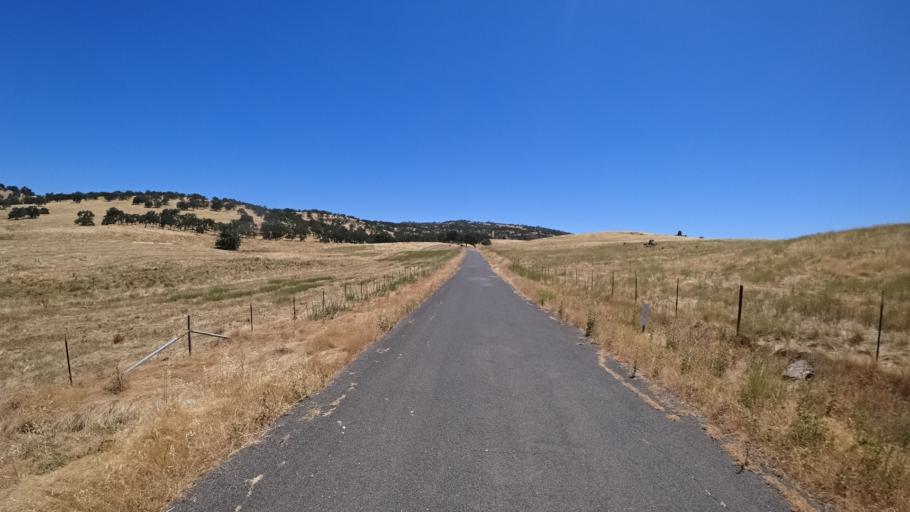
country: US
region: California
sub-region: Calaveras County
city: Rancho Calaveras
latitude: 38.0468
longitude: -120.8299
